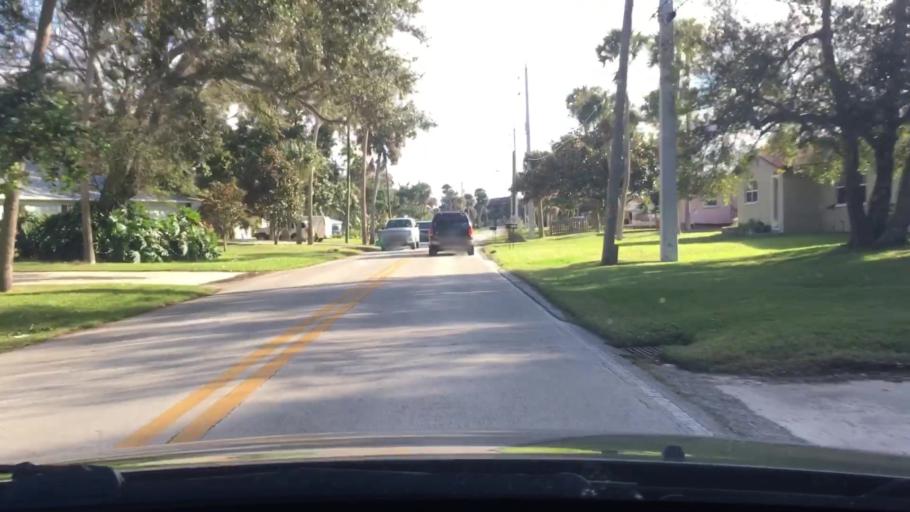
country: US
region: Florida
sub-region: Volusia County
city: Ormond-by-the-Sea
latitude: 29.3261
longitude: -81.0642
